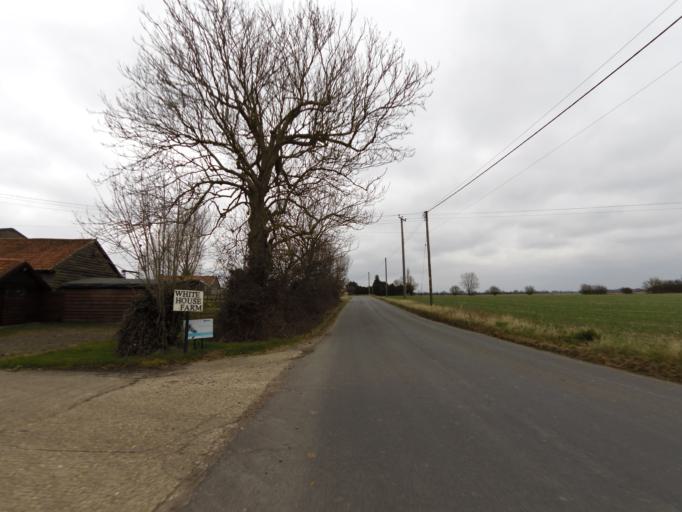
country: GB
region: England
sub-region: Suffolk
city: Ipswich
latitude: 52.1270
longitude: 1.1635
